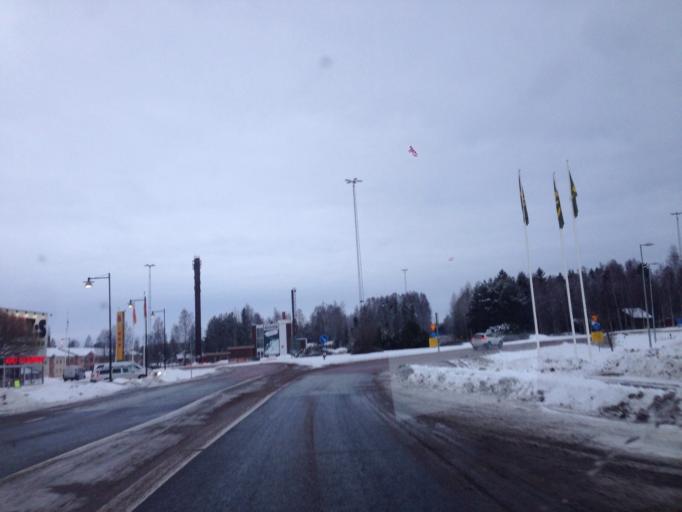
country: SE
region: Dalarna
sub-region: Mora Kommun
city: Mora
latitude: 61.0082
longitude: 14.5892
